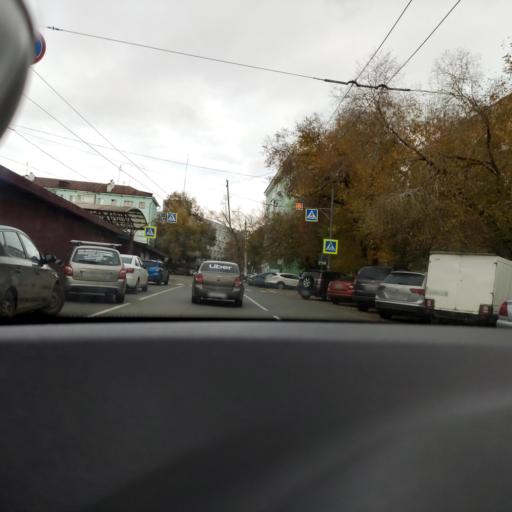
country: RU
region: Samara
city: Samara
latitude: 53.1942
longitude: 50.1265
